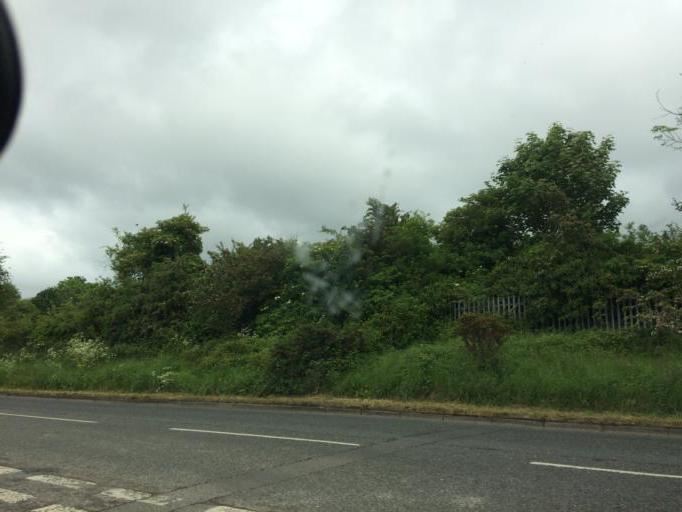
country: GB
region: Northern Ireland
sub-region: Antrim Borough
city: Antrim
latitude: 54.7120
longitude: -6.2104
